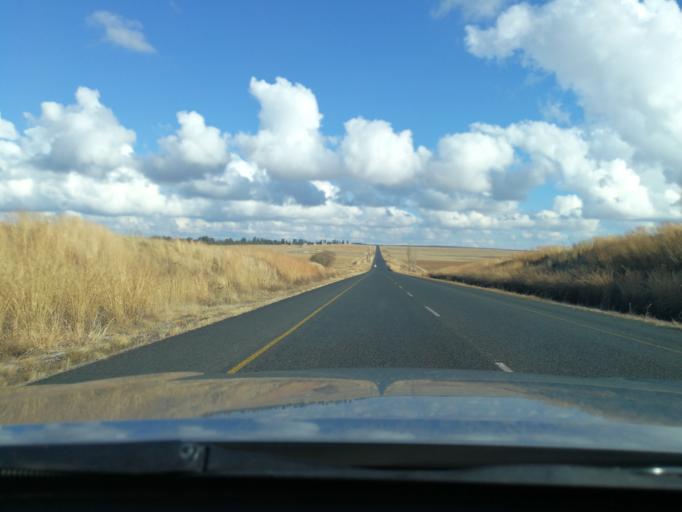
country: ZA
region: Orange Free State
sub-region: Thabo Mofutsanyana District Municipality
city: Bethlehem
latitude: -28.0995
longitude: 28.3519
